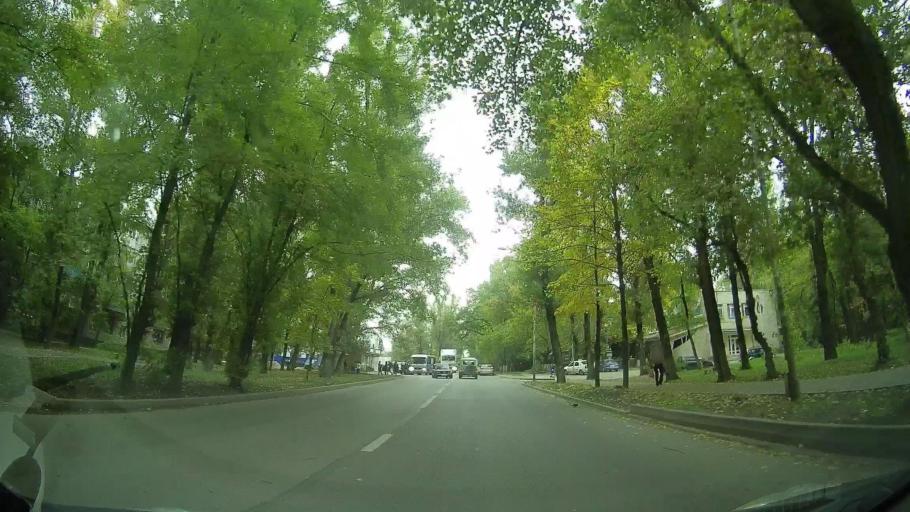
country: RU
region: Rostov
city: Severnyy
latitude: 47.2650
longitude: 39.6662
